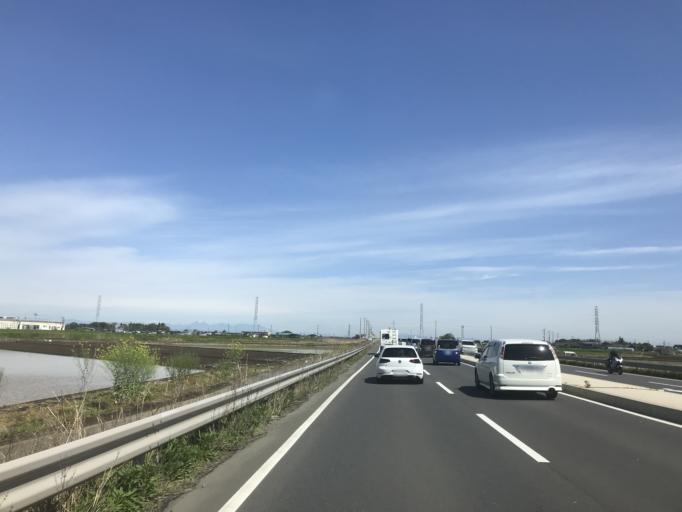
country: JP
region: Ibaraki
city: Ishige
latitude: 36.1642
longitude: 139.9946
